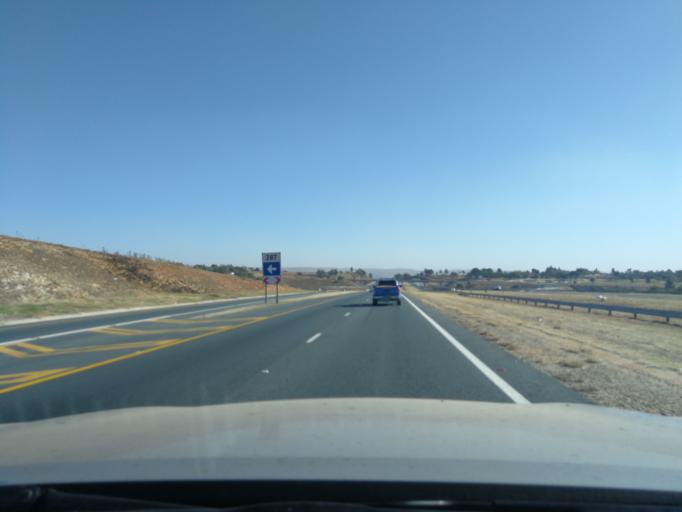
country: ZA
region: Gauteng
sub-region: West Rand District Municipality
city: Muldersdriseloop
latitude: -26.0174
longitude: 27.8677
